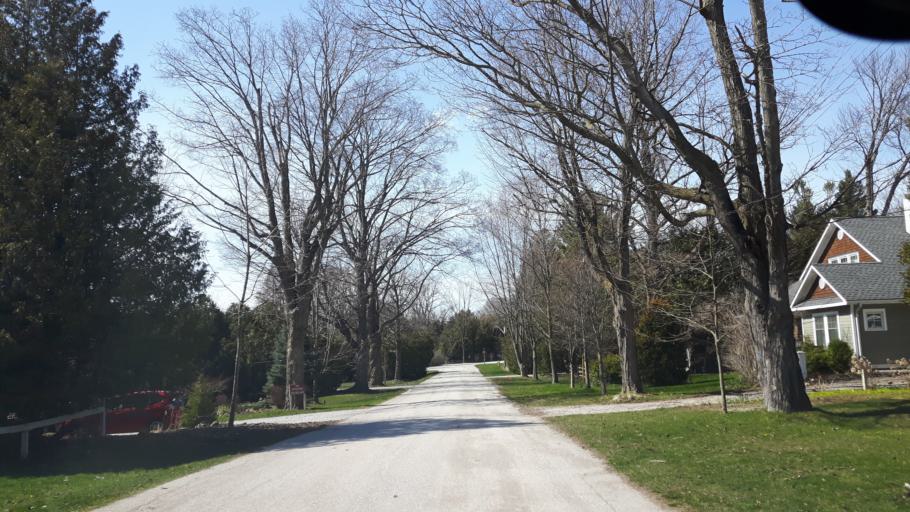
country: CA
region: Ontario
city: Bluewater
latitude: 43.5652
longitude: -81.7033
